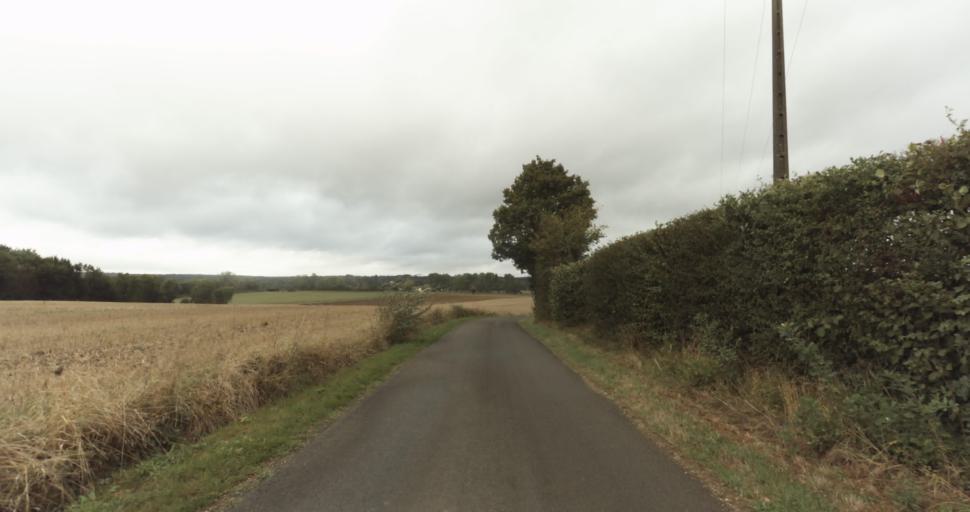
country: FR
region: Lower Normandy
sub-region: Departement de l'Orne
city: Sainte-Gauburge-Sainte-Colombe
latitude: 48.7369
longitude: 0.4700
